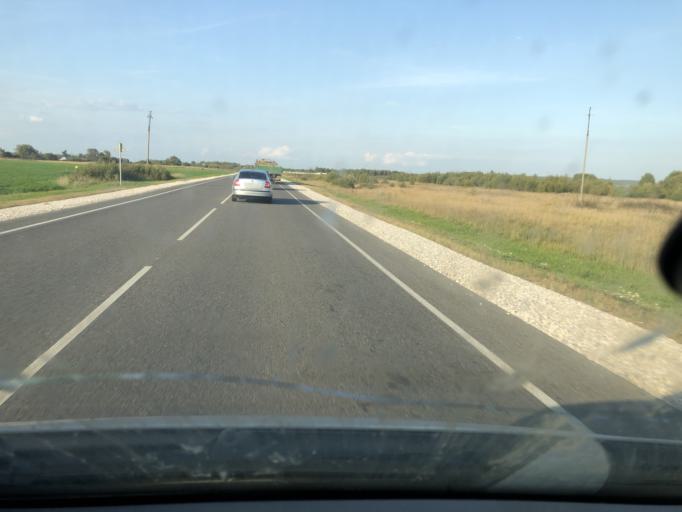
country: RU
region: Kaluga
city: Peremyshl'
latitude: 54.2577
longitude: 36.1270
